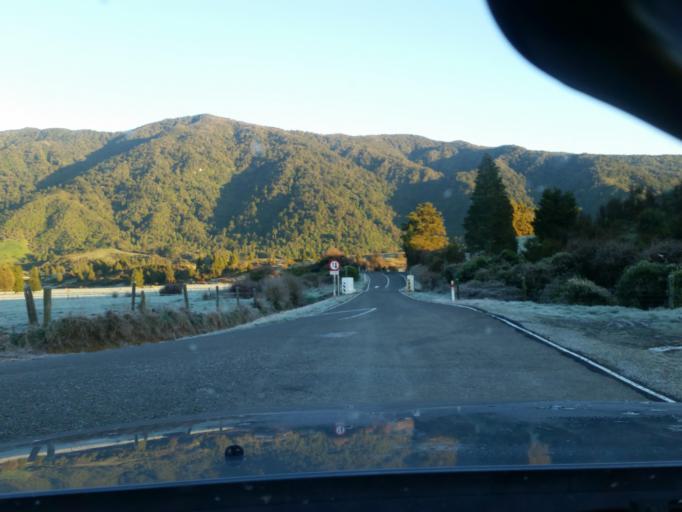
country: NZ
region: Tasman
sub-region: Tasman District
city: Takaka
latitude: -40.7574
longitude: 172.5634
